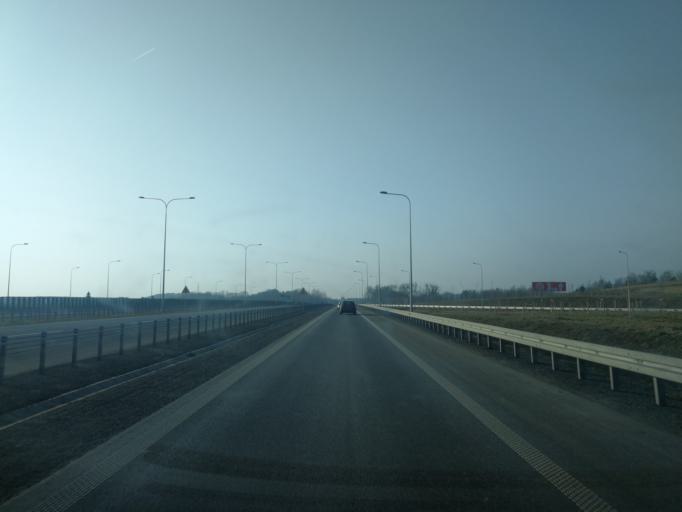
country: PL
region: Warmian-Masurian Voivodeship
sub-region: Powiat ostrodzki
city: Ostroda
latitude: 53.6857
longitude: 20.0057
